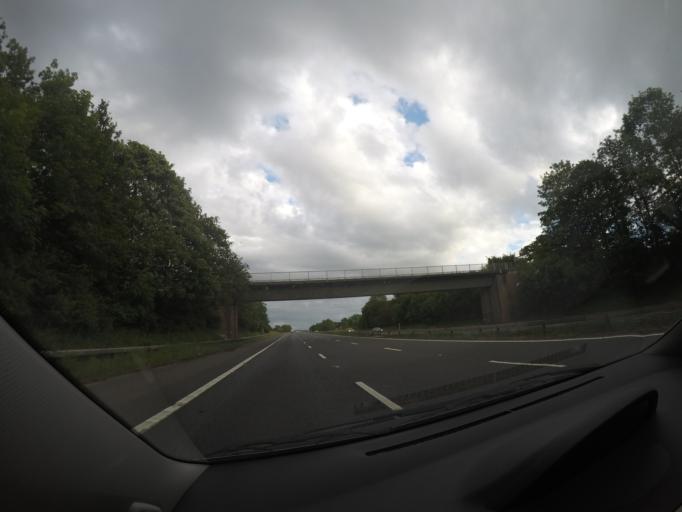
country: GB
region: England
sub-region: Cumbria
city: Penrith
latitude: 54.7469
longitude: -2.8130
